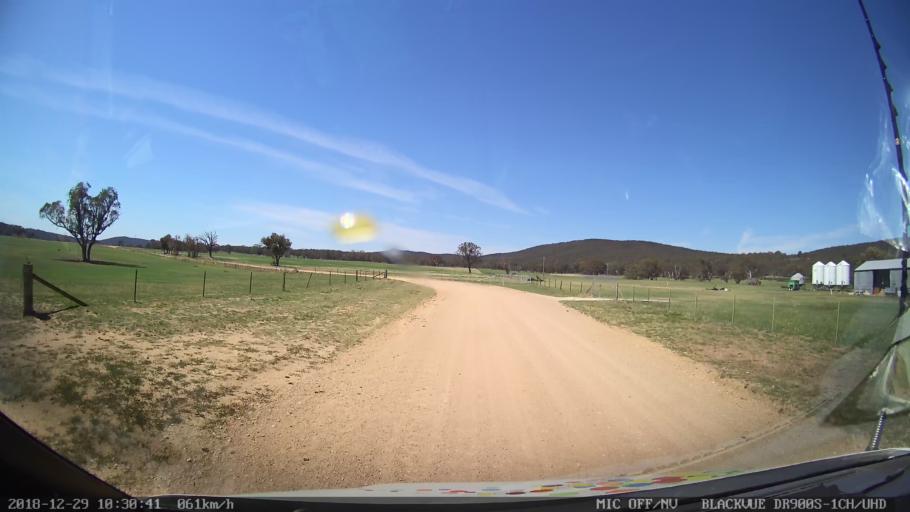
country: AU
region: New South Wales
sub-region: Yass Valley
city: Gundaroo
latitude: -34.9633
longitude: 149.4543
